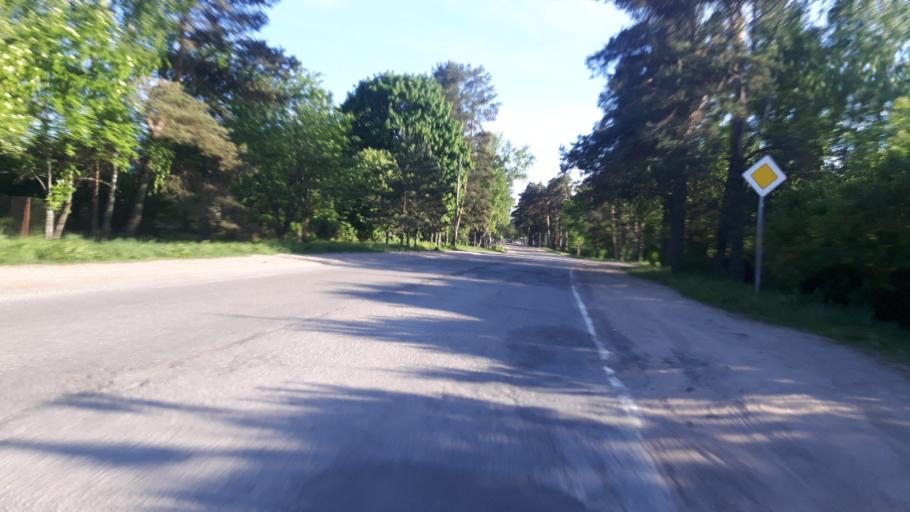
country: RU
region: Leningrad
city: Vistino
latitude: 59.7736
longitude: 28.4758
